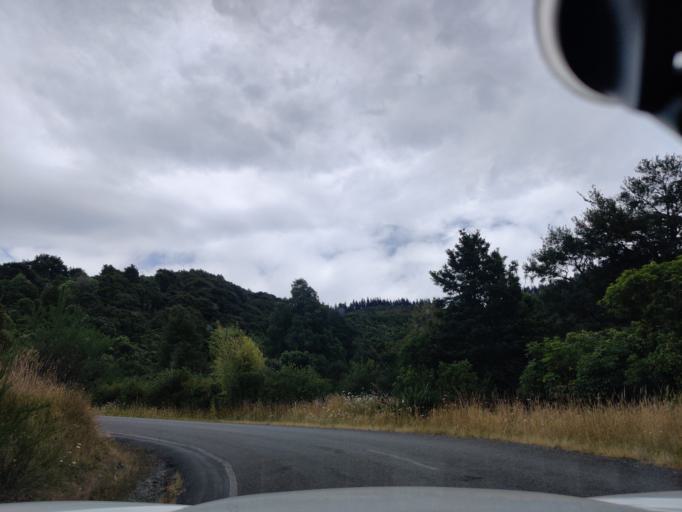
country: NZ
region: Wellington
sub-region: Masterton District
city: Masterton
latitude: -41.0367
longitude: 175.4185
